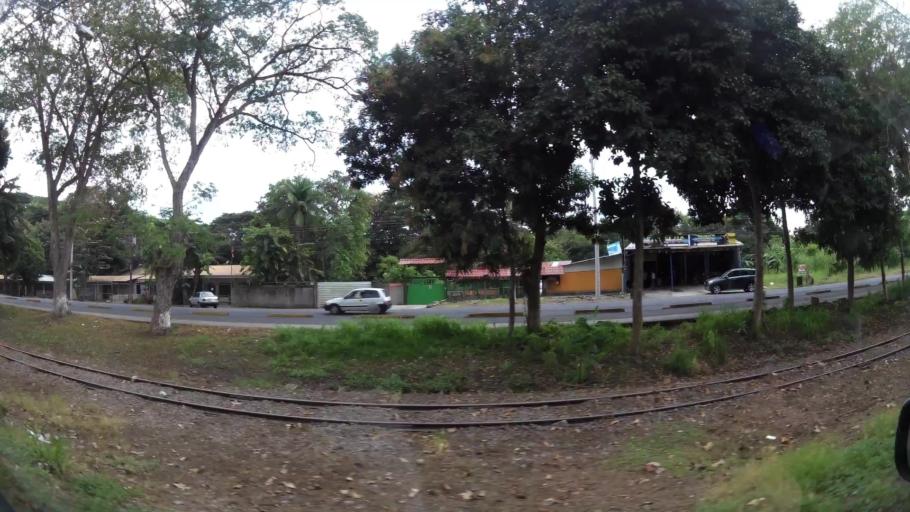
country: CR
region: Puntarenas
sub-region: Canton Central de Puntarenas
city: Chacarita
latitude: 9.9781
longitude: -84.7440
